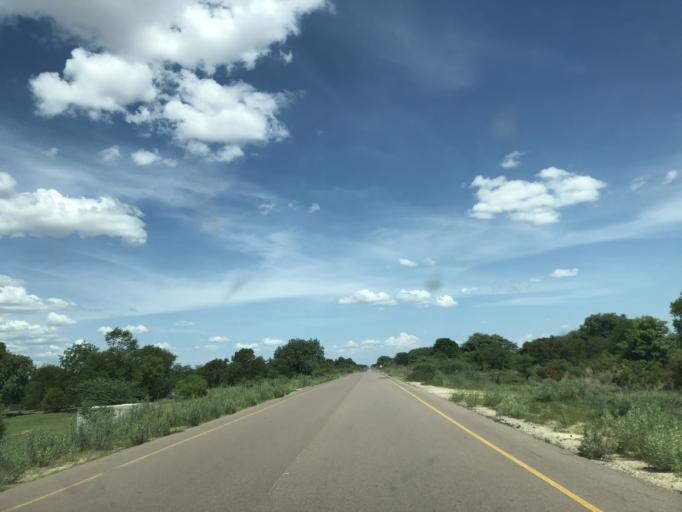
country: AO
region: Cunene
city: Ondjiva
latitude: -16.8979
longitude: 15.5065
